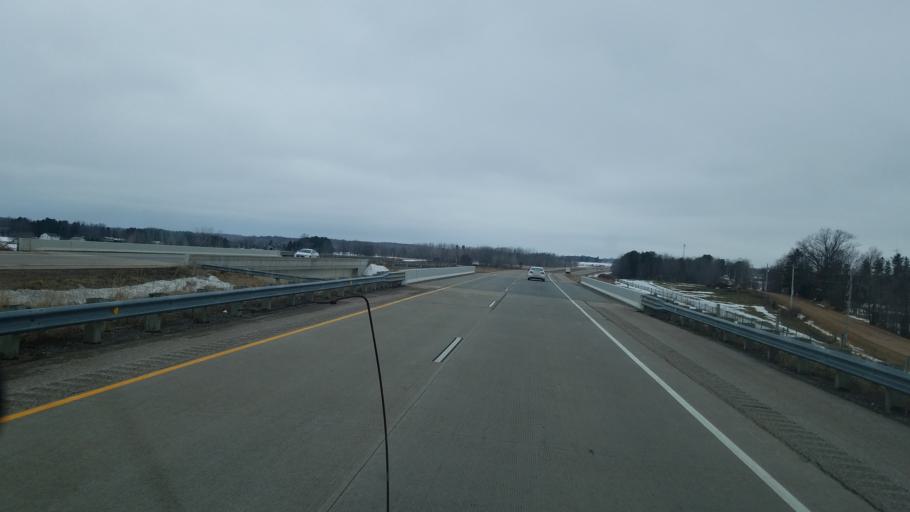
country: US
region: Wisconsin
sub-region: Marathon County
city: Mosinee
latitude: 44.5980
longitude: -89.7663
